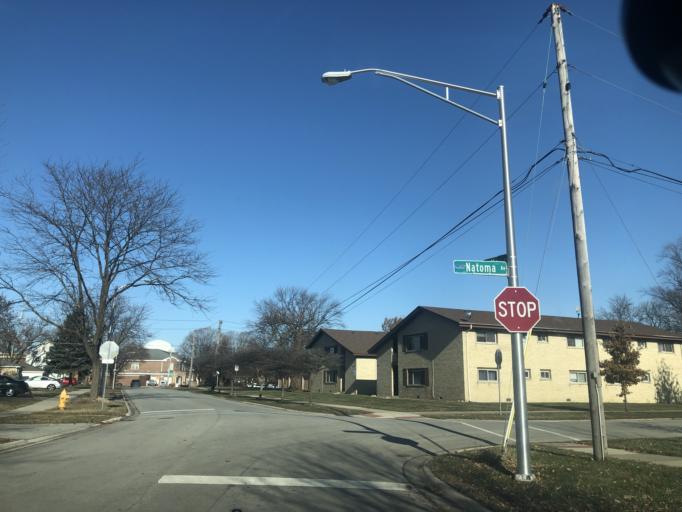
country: US
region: Illinois
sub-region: DuPage County
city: Addison
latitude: 41.9303
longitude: -87.9922
